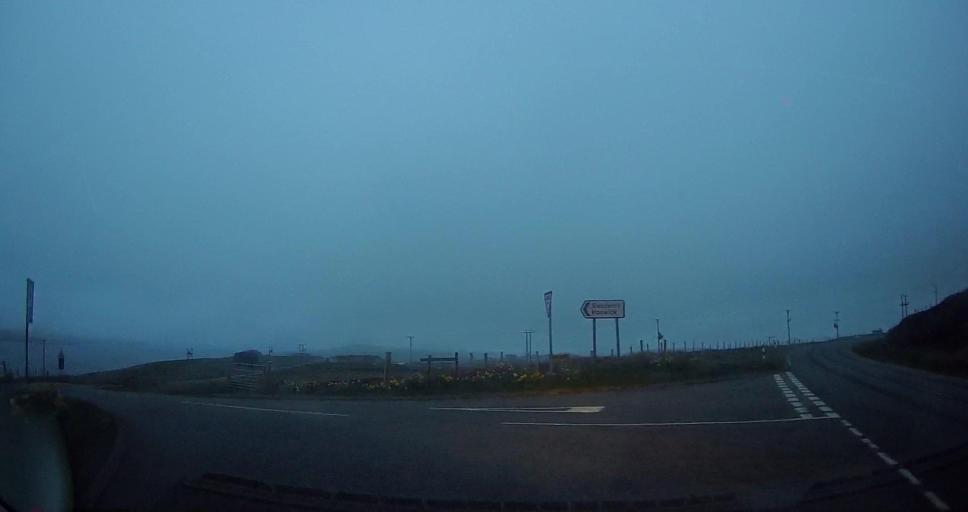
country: GB
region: Scotland
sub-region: Shetland Islands
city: Sandwick
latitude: 60.0179
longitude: -1.2311
